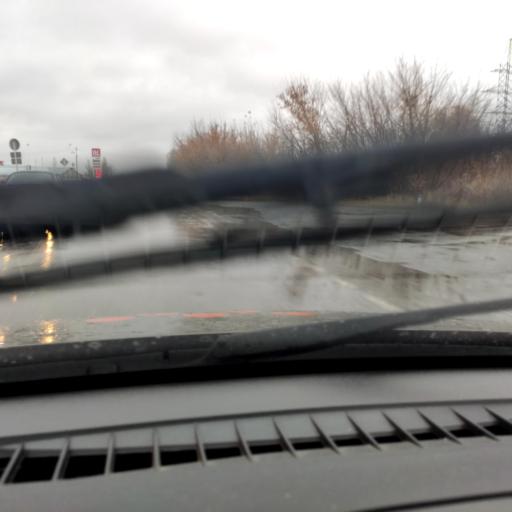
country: RU
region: Samara
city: Tol'yatti
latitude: 53.6320
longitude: 49.3022
